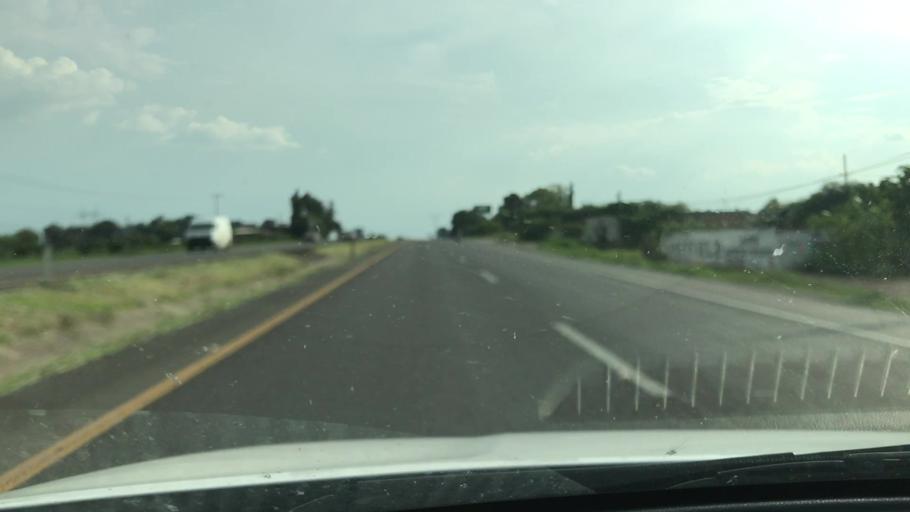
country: MX
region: Guanajuato
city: Penjamo
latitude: 20.4061
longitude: -101.7423
